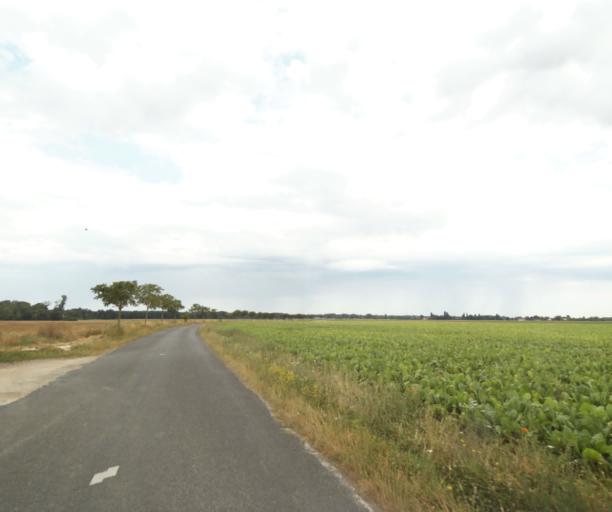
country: FR
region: Ile-de-France
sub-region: Departement de Seine-et-Marne
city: Arbonne-la-Foret
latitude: 48.4244
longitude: 2.5618
